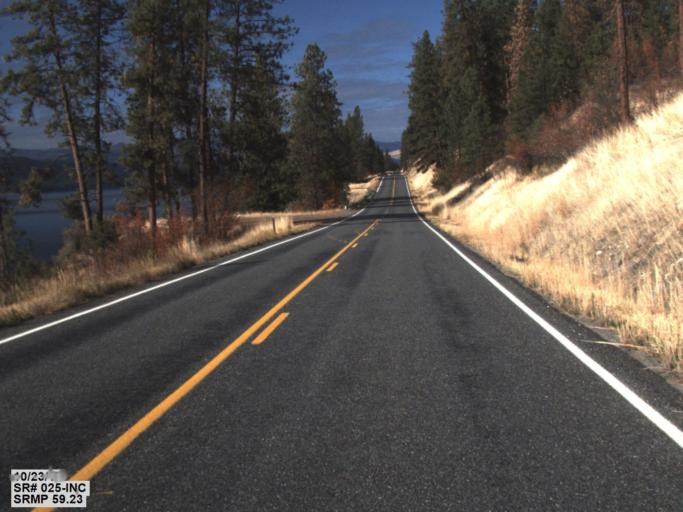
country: US
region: Washington
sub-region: Stevens County
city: Kettle Falls
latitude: 48.3277
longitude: -118.1533
